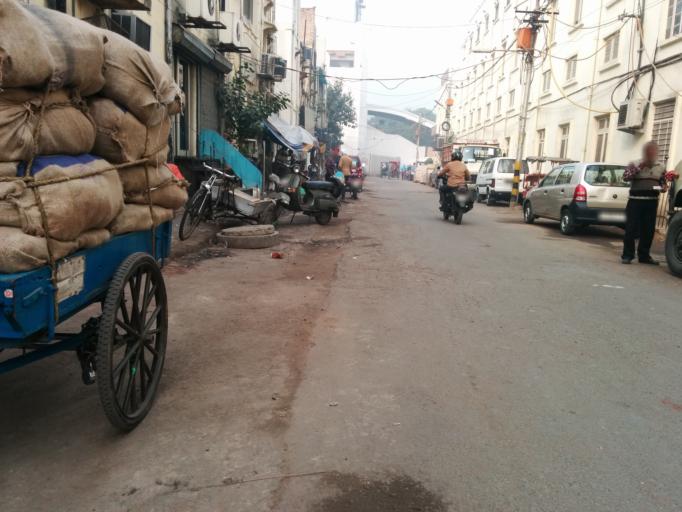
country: IN
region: NCT
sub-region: New Delhi
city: New Delhi
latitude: 28.6392
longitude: 77.2094
